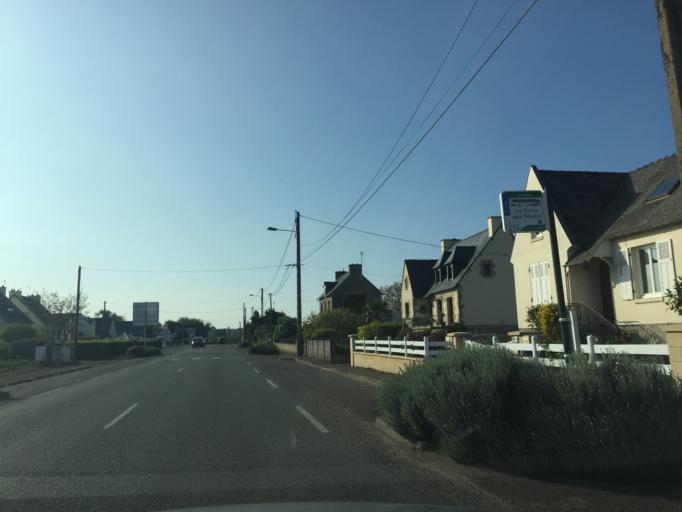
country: FR
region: Brittany
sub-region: Departement des Cotes-d'Armor
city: Crehen
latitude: 48.5835
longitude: -2.2354
